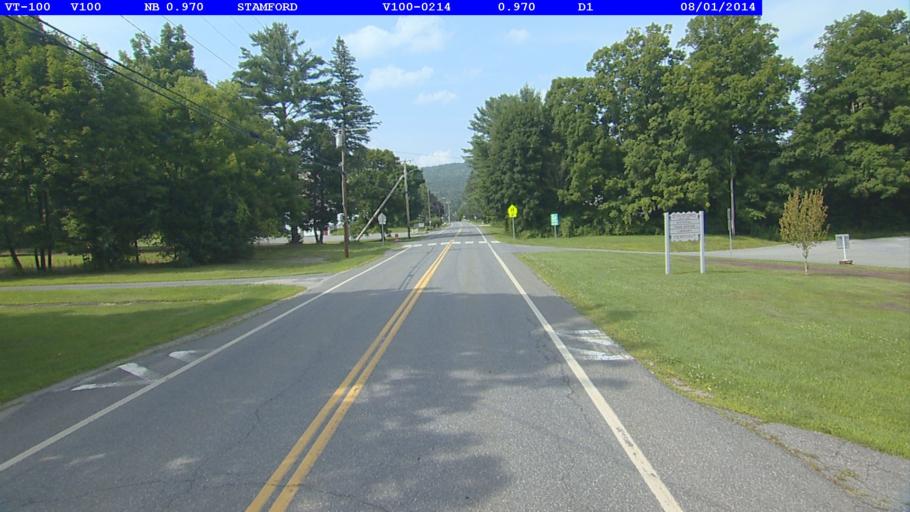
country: US
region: Massachusetts
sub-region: Berkshire County
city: North Adams
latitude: 42.7546
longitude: -73.0682
